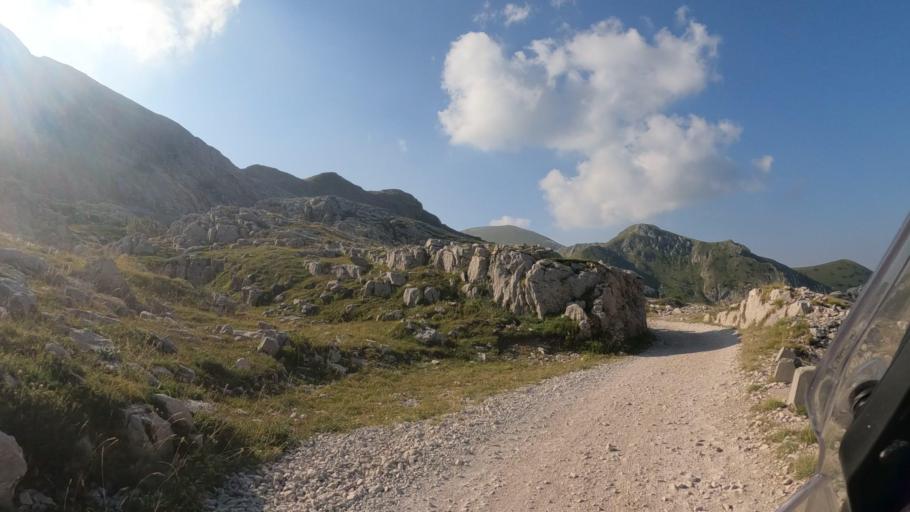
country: IT
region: Piedmont
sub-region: Provincia di Cuneo
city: Limone Piemonte
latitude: 44.1659
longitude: 7.6685
